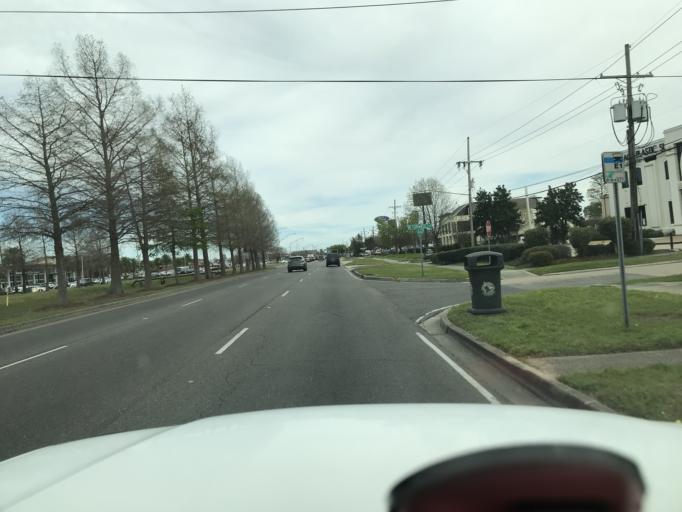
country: US
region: Louisiana
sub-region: Jefferson Parish
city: Metairie
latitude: 30.0038
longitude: -90.1688
